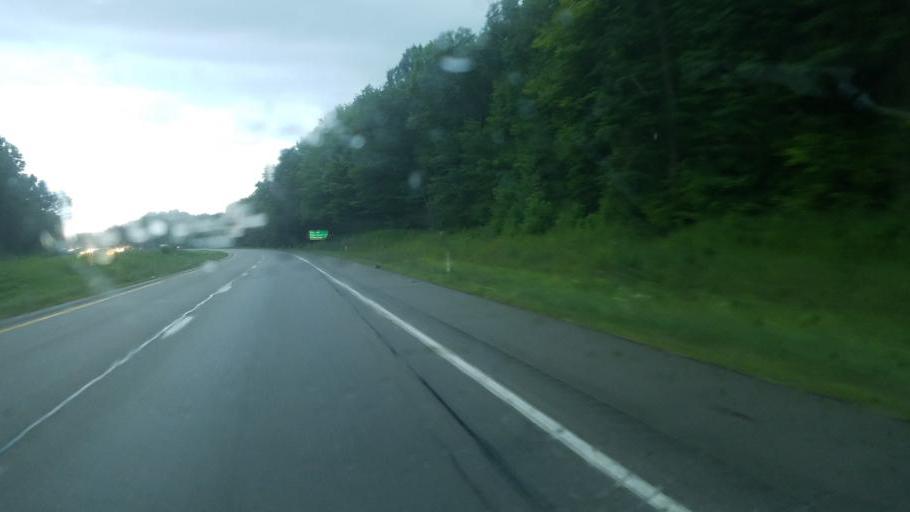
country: US
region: Pennsylvania
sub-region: Mercer County
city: Grove City
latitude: 41.1301
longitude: -80.1534
